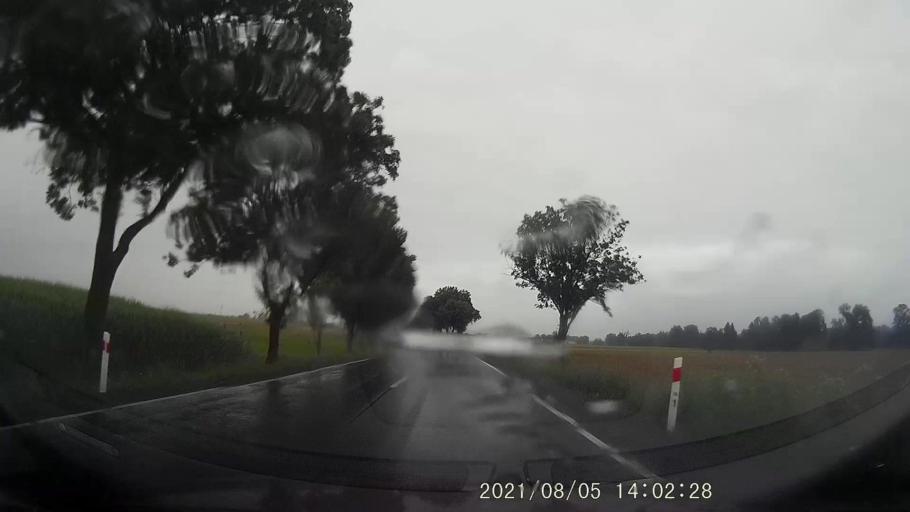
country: PL
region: Opole Voivodeship
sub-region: Powiat krapkowicki
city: Strzeleczki
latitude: 50.4554
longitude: 17.8749
